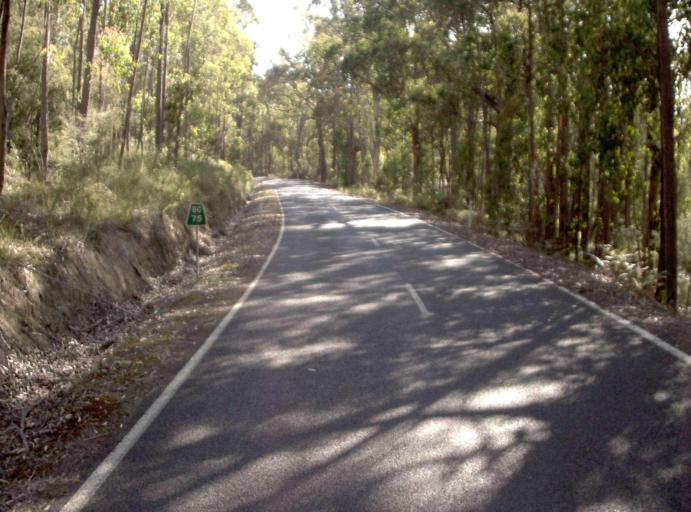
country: AU
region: Victoria
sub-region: East Gippsland
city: Lakes Entrance
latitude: -37.5818
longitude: 148.5383
